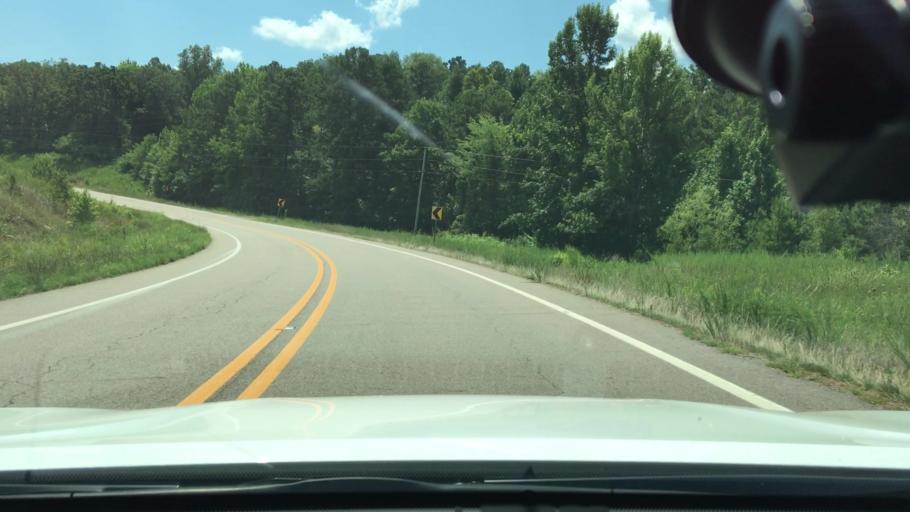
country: US
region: Arkansas
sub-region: Logan County
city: Paris
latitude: 35.2571
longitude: -93.6828
